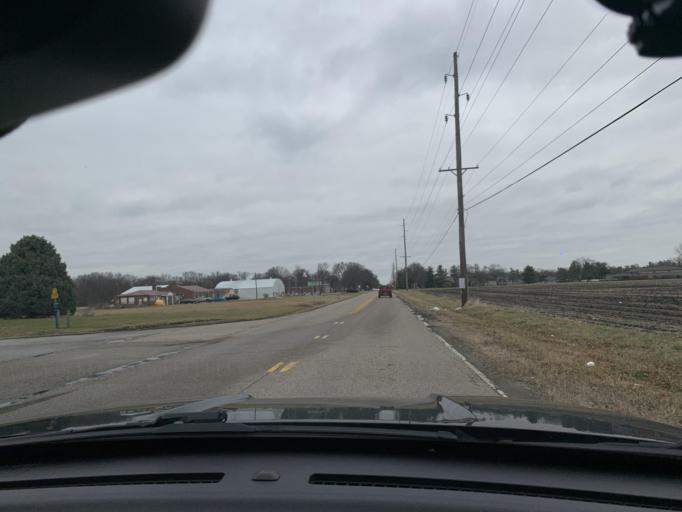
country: US
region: Illinois
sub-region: Sangamon County
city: Jerome
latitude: 39.7534
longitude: -89.6866
